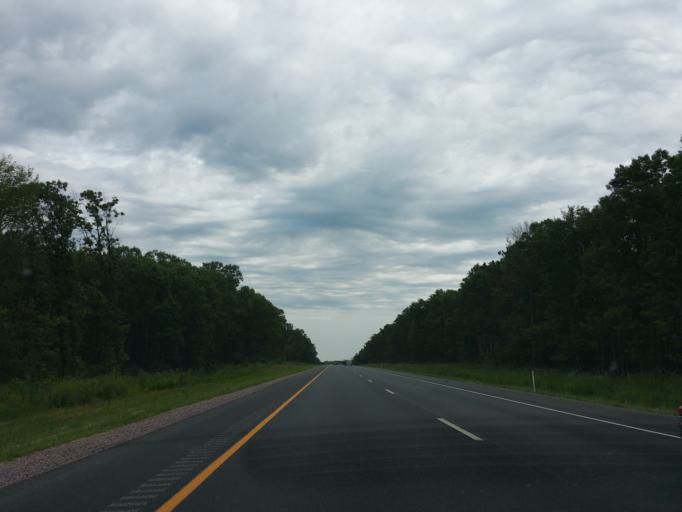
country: US
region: Wisconsin
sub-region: Juneau County
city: Mauston
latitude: 43.7517
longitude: -89.9545
